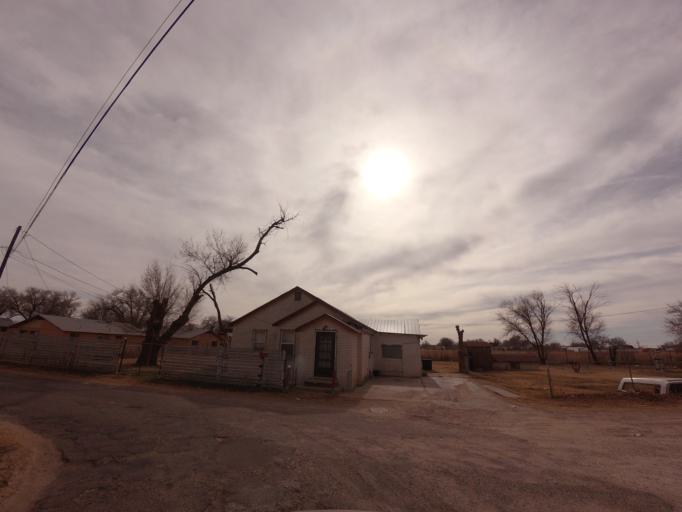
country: US
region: New Mexico
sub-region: Curry County
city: Clovis
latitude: 34.4080
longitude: -103.2337
